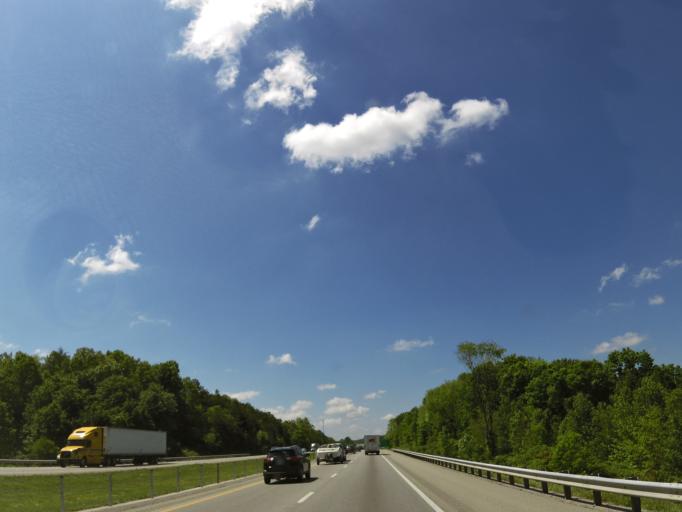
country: US
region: Kentucky
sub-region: Laurel County
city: North Corbin
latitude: 37.0106
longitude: -84.1029
